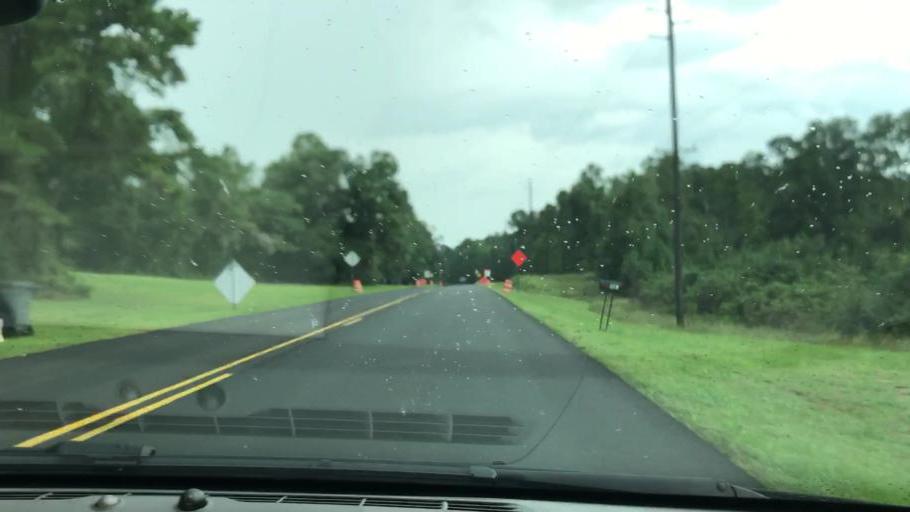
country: US
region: Georgia
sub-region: Clay County
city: Fort Gaines
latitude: 31.5257
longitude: -85.0237
